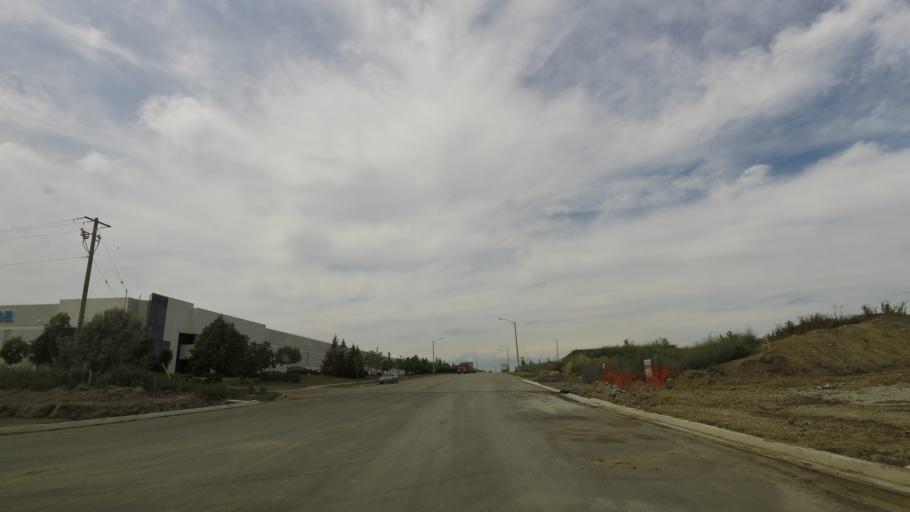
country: CA
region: Ontario
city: Mississauga
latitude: 43.6319
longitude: -79.6924
